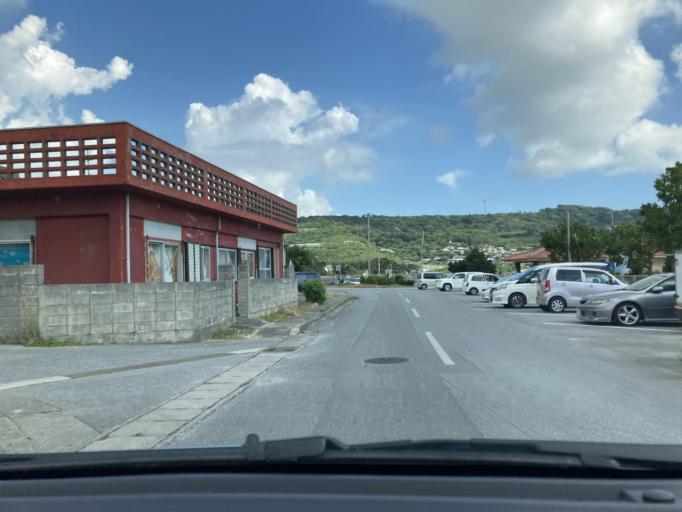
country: JP
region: Okinawa
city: Itoman
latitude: 26.1309
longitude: 127.7740
